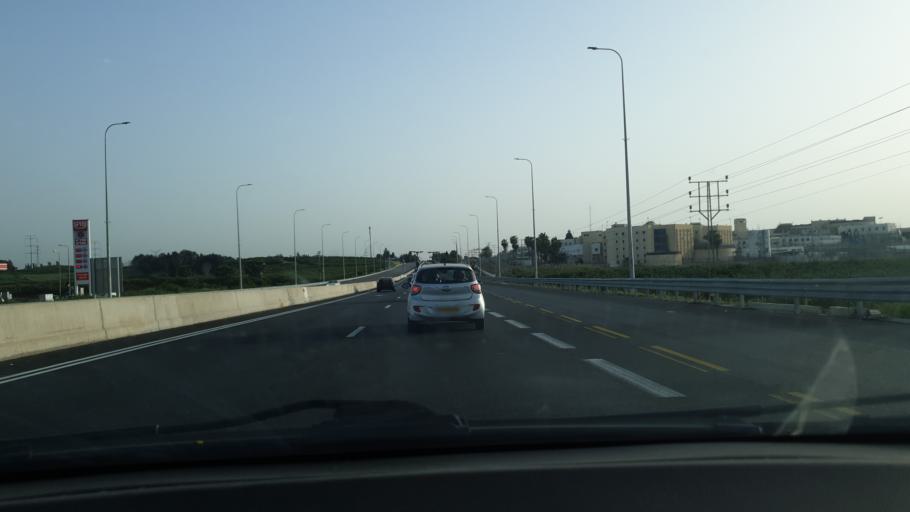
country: IL
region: Central District
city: Even Yehuda
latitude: 32.2444
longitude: 34.8879
